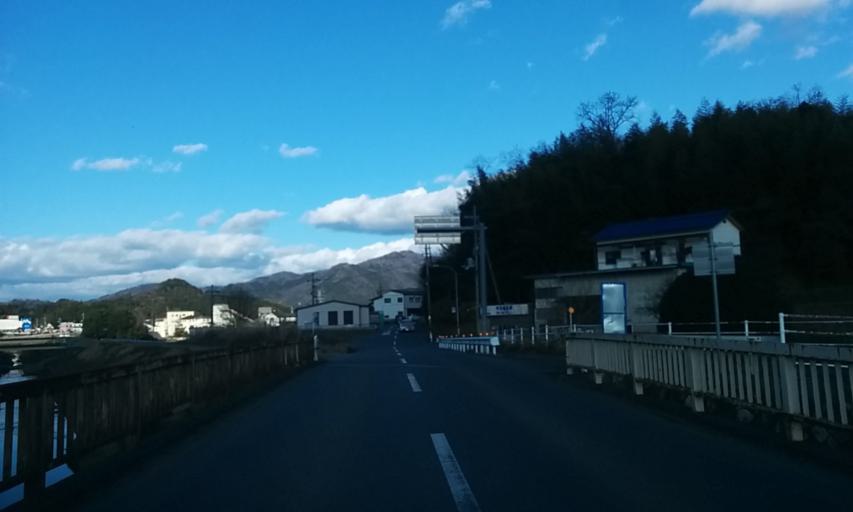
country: JP
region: Kyoto
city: Fukuchiyama
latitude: 35.3045
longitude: 135.1009
